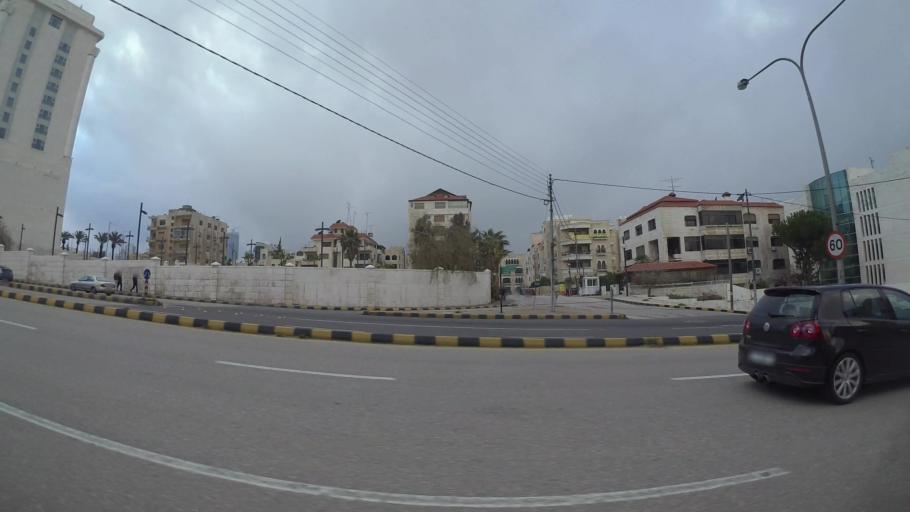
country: JO
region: Amman
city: Amman
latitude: 31.9624
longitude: 35.8824
